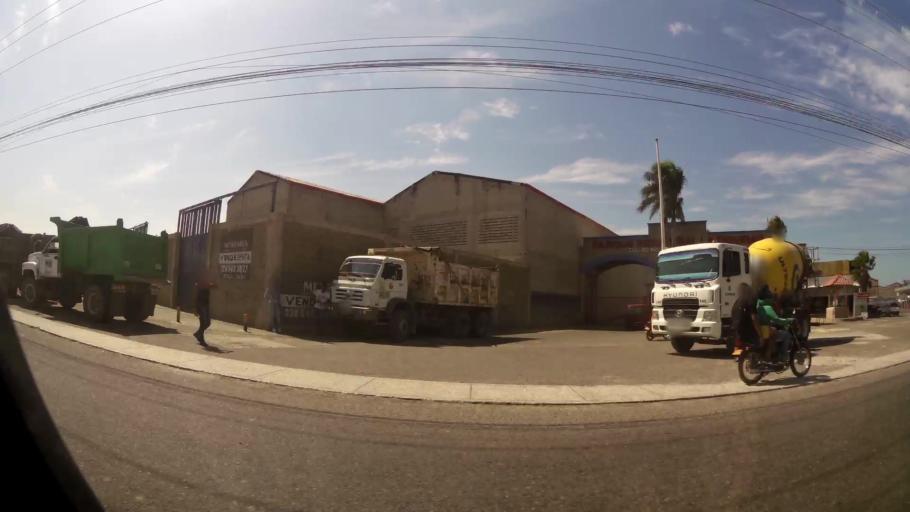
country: CO
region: Atlantico
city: Barranquilla
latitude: 10.9672
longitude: -74.8385
